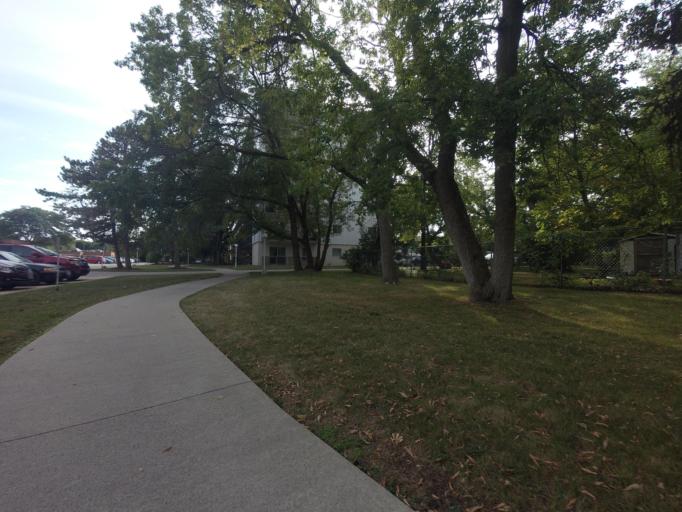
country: CA
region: Ontario
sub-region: Wellington County
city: Guelph
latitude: 43.5554
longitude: -80.2647
